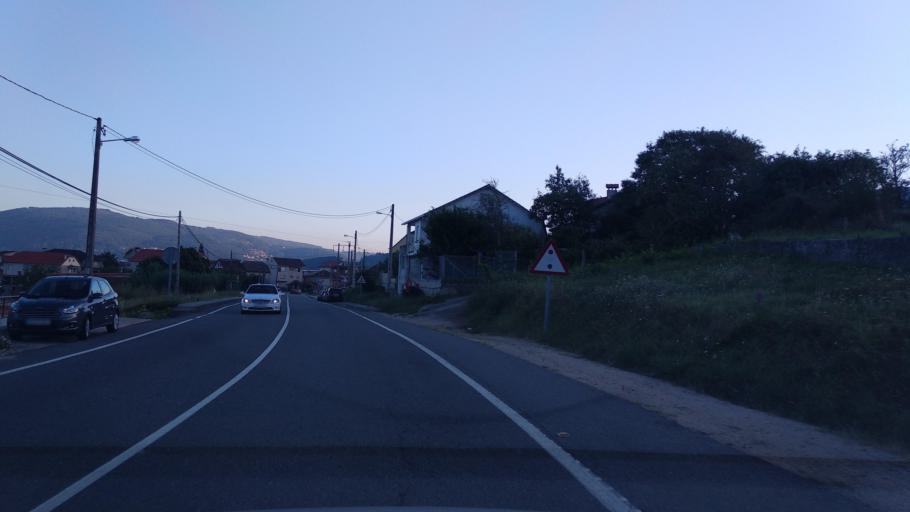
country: ES
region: Galicia
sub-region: Provincia de Pontevedra
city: Redondela
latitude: 42.3244
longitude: -8.6514
